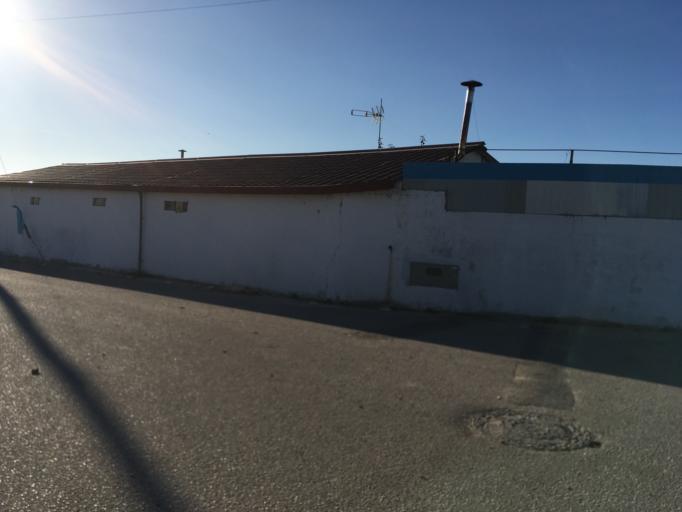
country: PT
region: Aveiro
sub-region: Estarreja
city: Salreu
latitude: 40.7331
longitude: -8.5664
